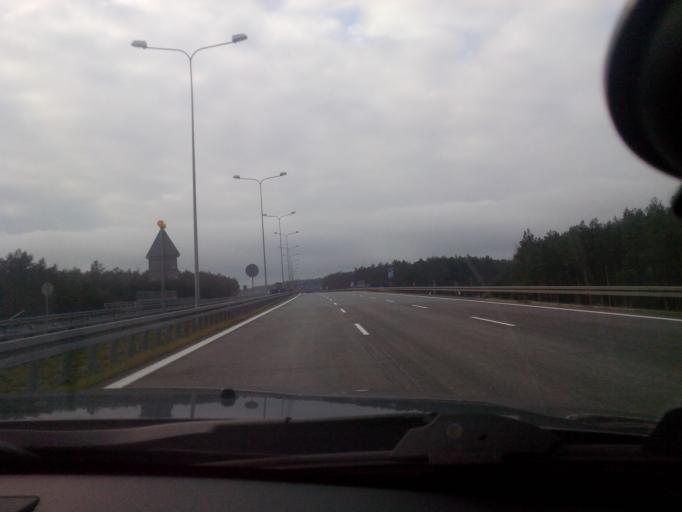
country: PL
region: Lubusz
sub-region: Powiat slubicki
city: Rzepin
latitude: 52.3351
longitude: 14.8927
